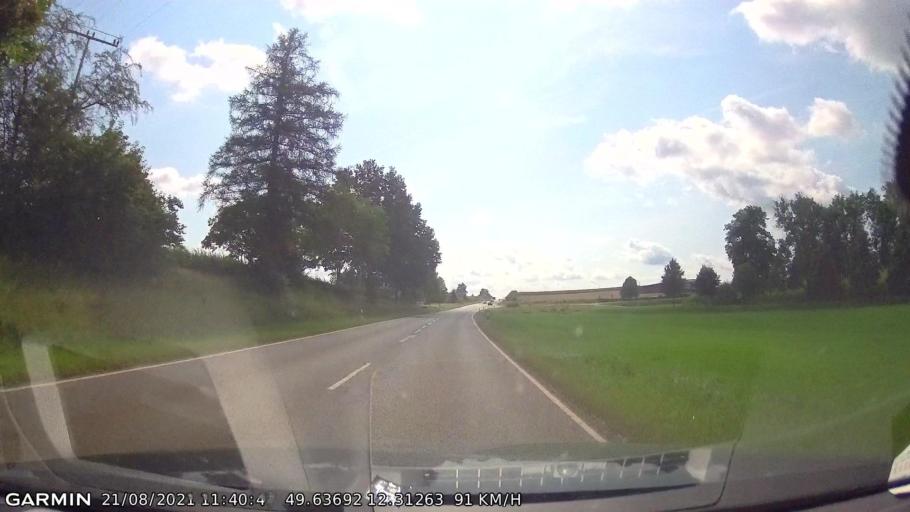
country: DE
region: Bavaria
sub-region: Upper Palatinate
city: Vohenstrauss
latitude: 49.6368
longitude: 12.3127
